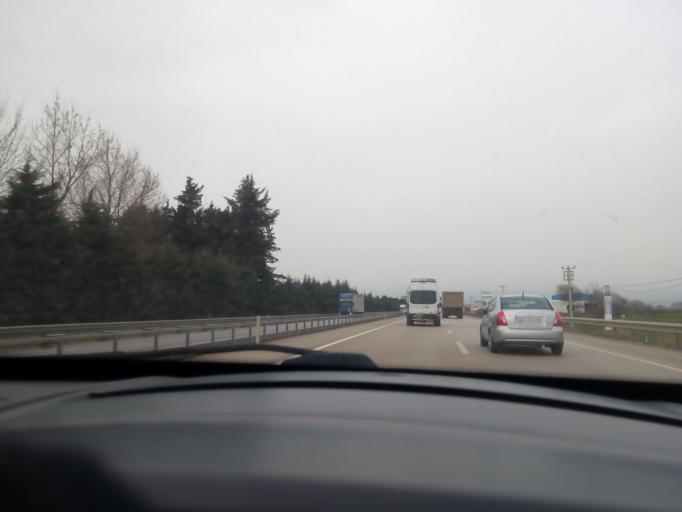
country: TR
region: Bursa
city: Tatkavakli
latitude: 40.0318
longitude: 28.3519
